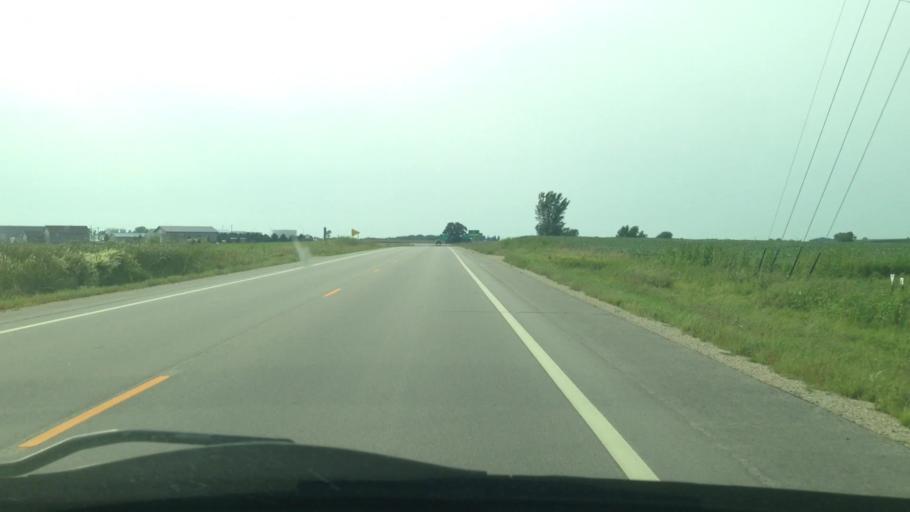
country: US
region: Minnesota
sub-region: Olmsted County
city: Eyota
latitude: 43.9964
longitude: -92.2390
